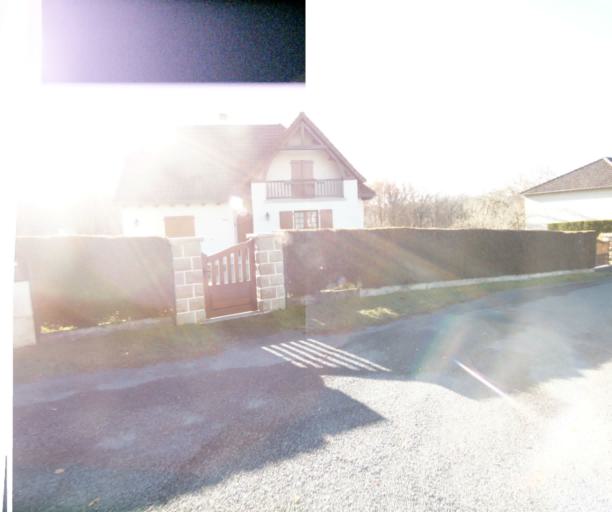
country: FR
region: Limousin
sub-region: Departement de la Correze
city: Chameyrat
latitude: 45.2363
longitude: 1.7368
